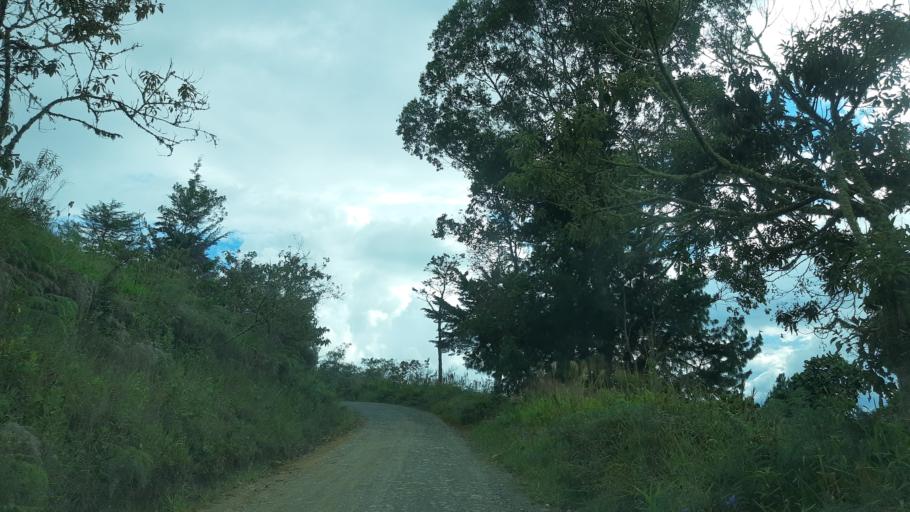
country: CO
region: Boyaca
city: Garagoa
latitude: 5.0065
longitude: -73.3413
